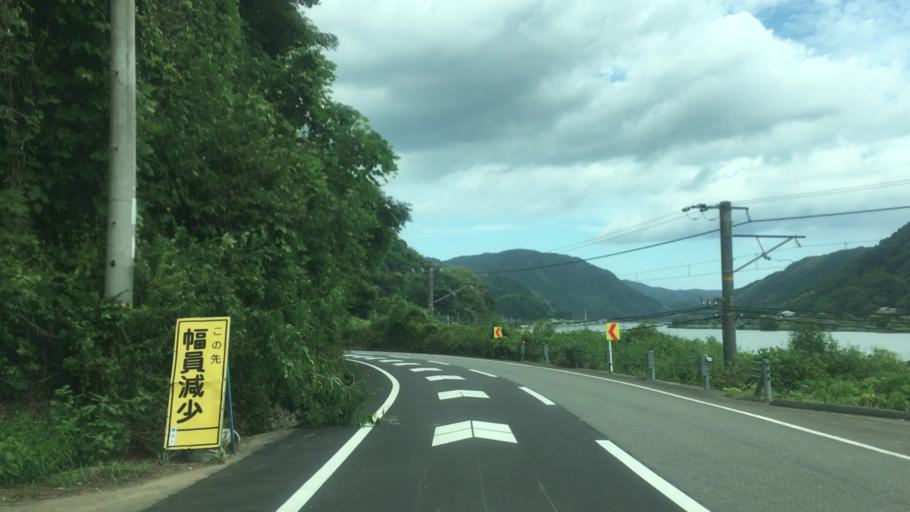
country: JP
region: Hyogo
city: Toyooka
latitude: 35.5796
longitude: 134.7999
